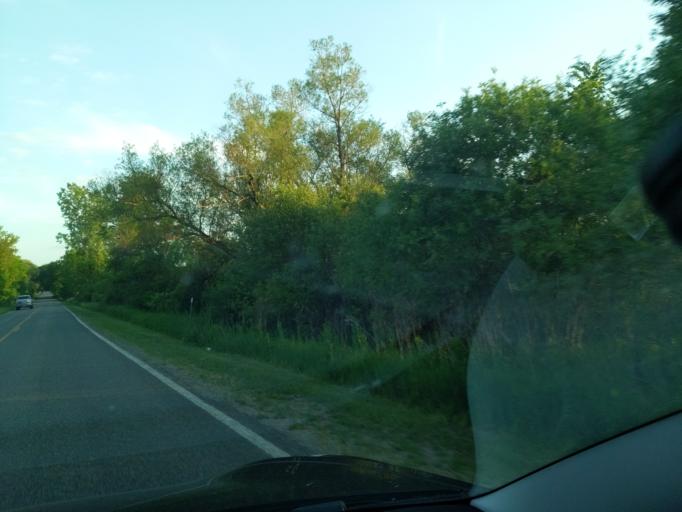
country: US
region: Michigan
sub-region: Barry County
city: Nashville
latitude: 42.5429
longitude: -85.0938
